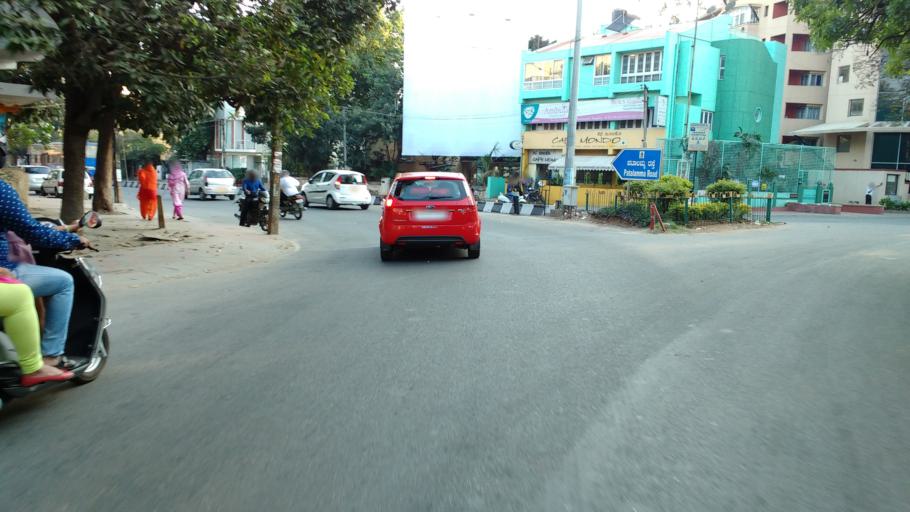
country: IN
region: Karnataka
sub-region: Bangalore Urban
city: Bangalore
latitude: 12.9400
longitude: 77.5777
